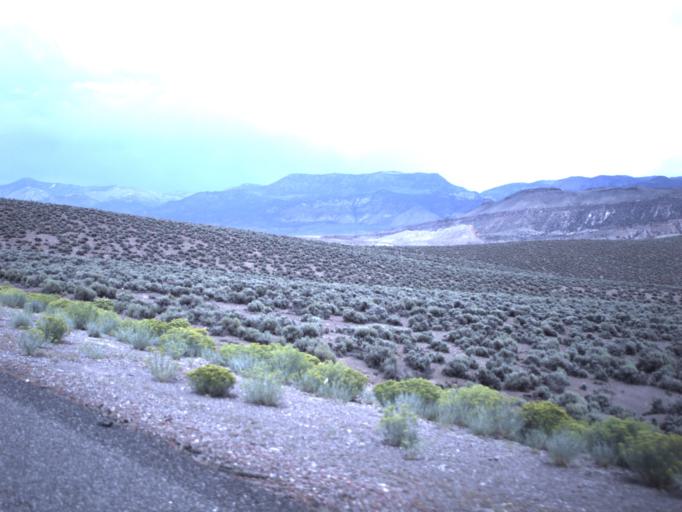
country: US
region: Utah
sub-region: Piute County
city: Junction
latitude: 38.3068
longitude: -112.2231
